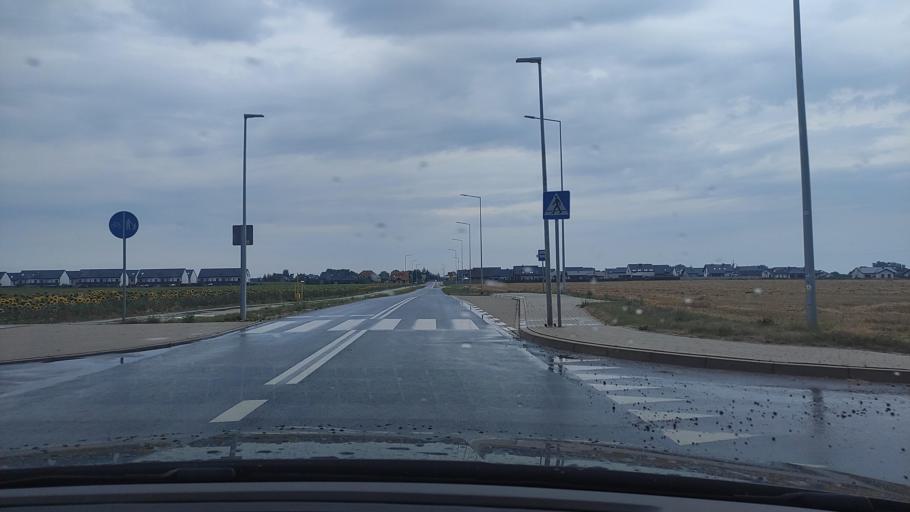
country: PL
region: Greater Poland Voivodeship
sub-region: Powiat poznanski
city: Kornik
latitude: 52.2966
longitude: 17.0985
